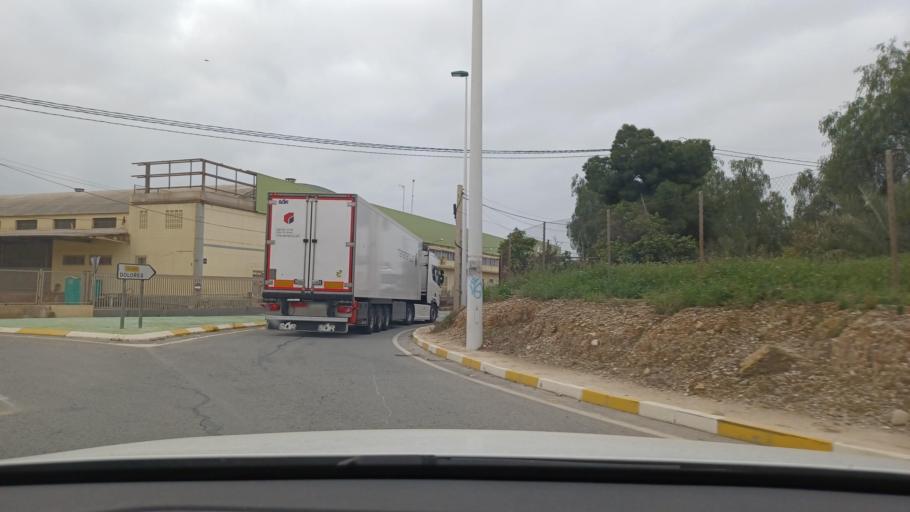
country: ES
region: Valencia
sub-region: Provincia de Alicante
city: Elche
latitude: 38.2448
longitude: -0.7067
